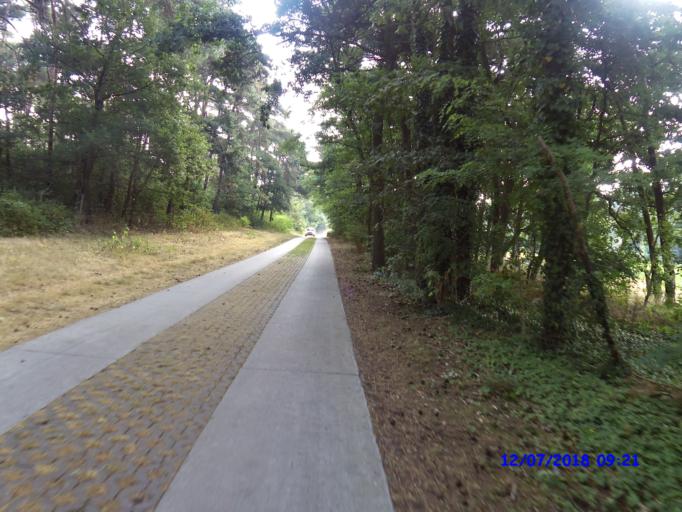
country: BE
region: Flanders
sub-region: Provincie Antwerpen
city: Mol
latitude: 51.1667
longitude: 5.1132
